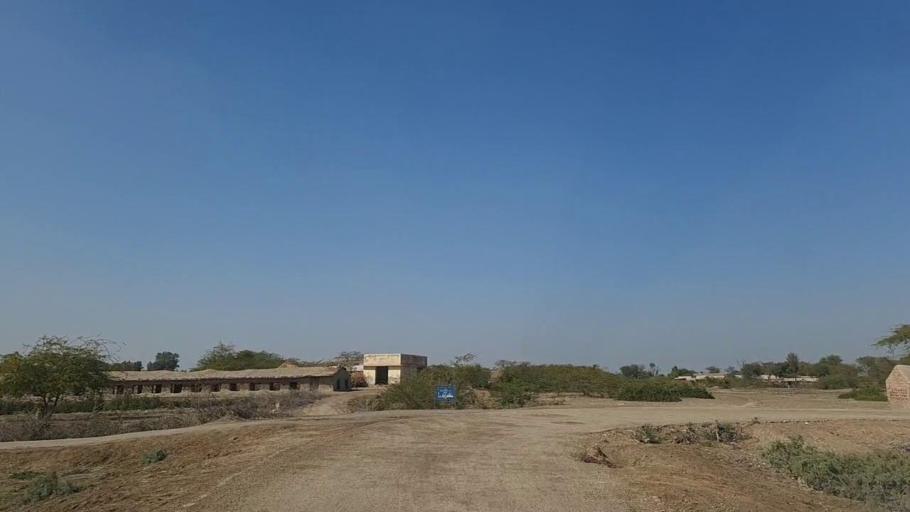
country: PK
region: Sindh
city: Samaro
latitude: 25.3988
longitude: 69.4000
